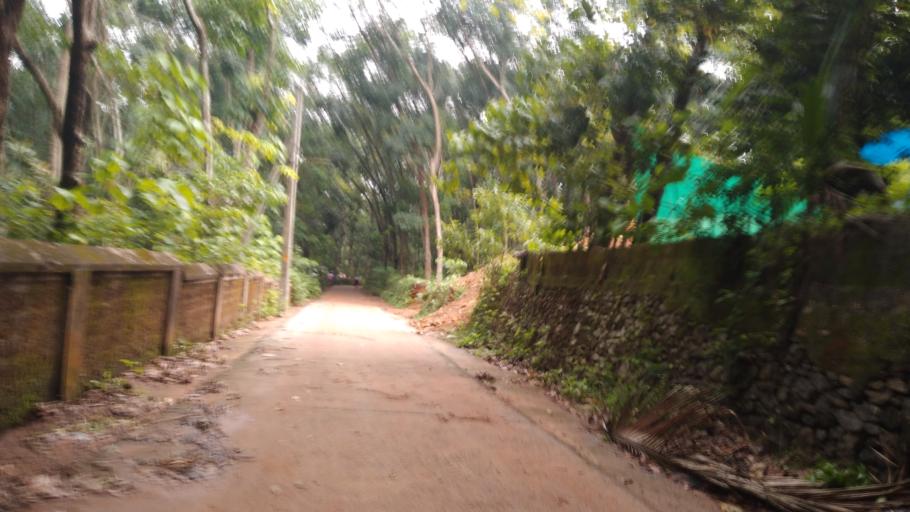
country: IN
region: Kerala
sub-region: Ernakulam
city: Kotamangalam
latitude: 10.1224
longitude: 76.5789
